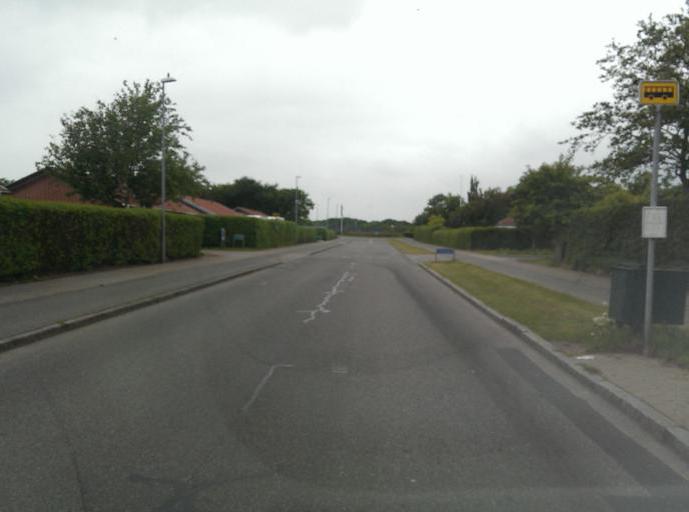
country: DK
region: South Denmark
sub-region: Fano Kommune
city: Nordby
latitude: 55.5323
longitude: 8.3634
